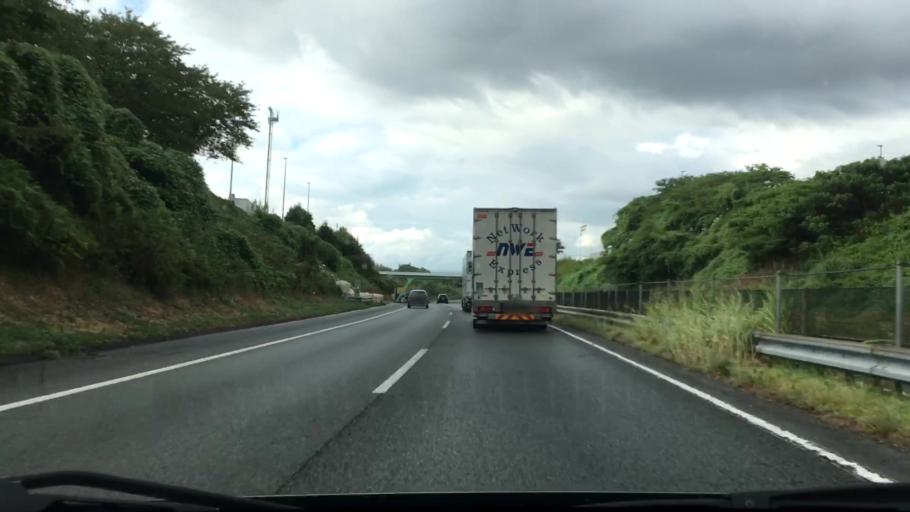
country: JP
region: Fukuoka
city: Koga
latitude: 33.7370
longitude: 130.5179
